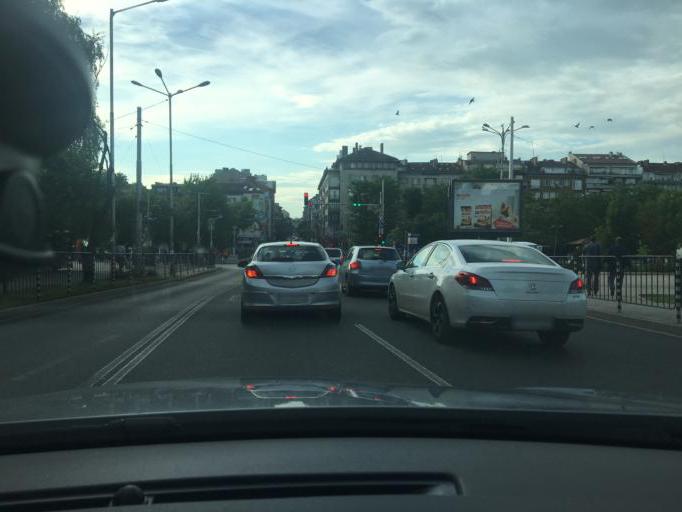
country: BG
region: Sofia-Capital
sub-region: Stolichna Obshtina
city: Sofia
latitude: 42.6857
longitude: 23.3318
